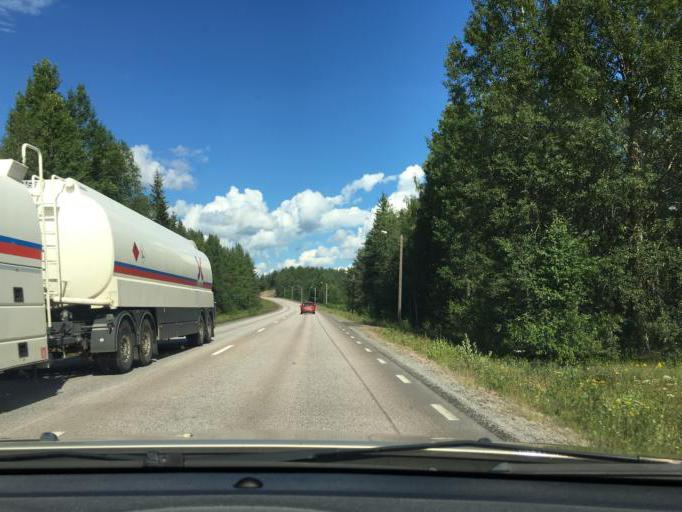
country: SE
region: Norrbotten
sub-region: Overkalix Kommun
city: OEverkalix
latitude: 66.2814
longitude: 22.8187
